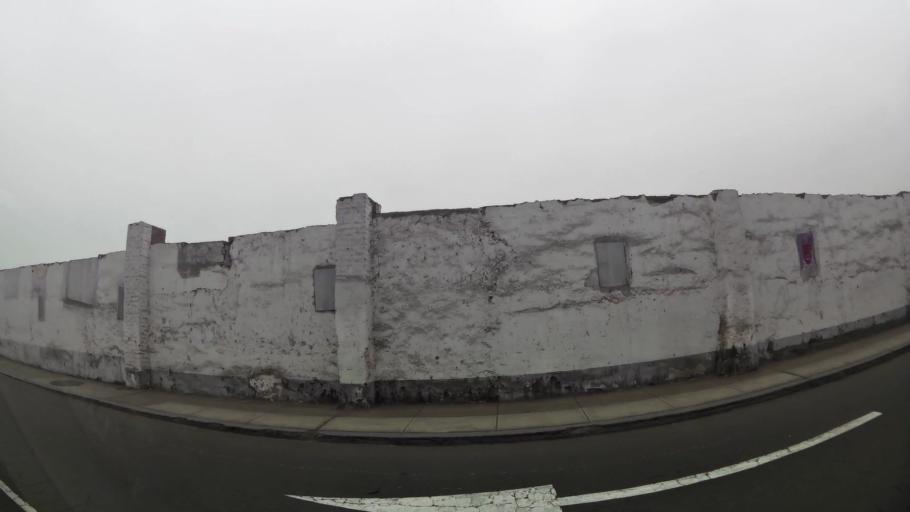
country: PE
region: Lima
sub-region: Lima
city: San Isidro
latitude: -12.1095
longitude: -77.0505
